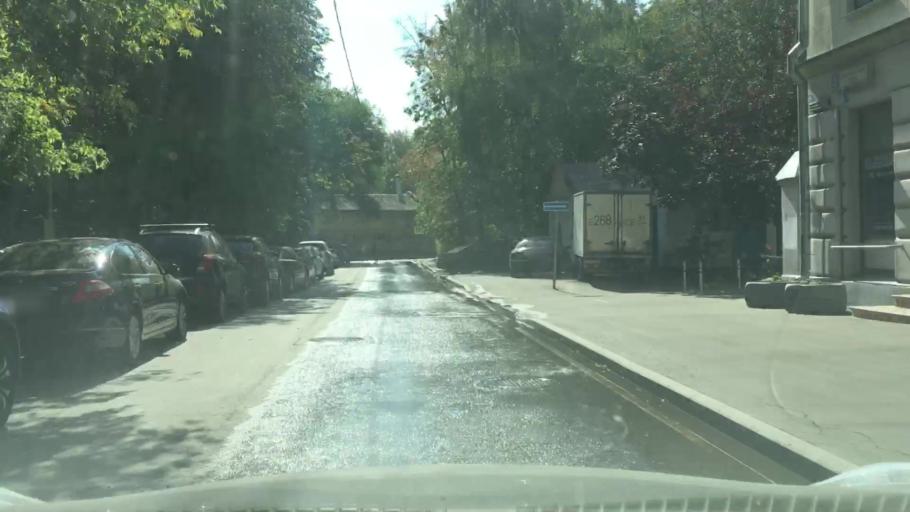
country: RU
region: Moskovskaya
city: Dorogomilovo
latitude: 55.7313
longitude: 37.5841
